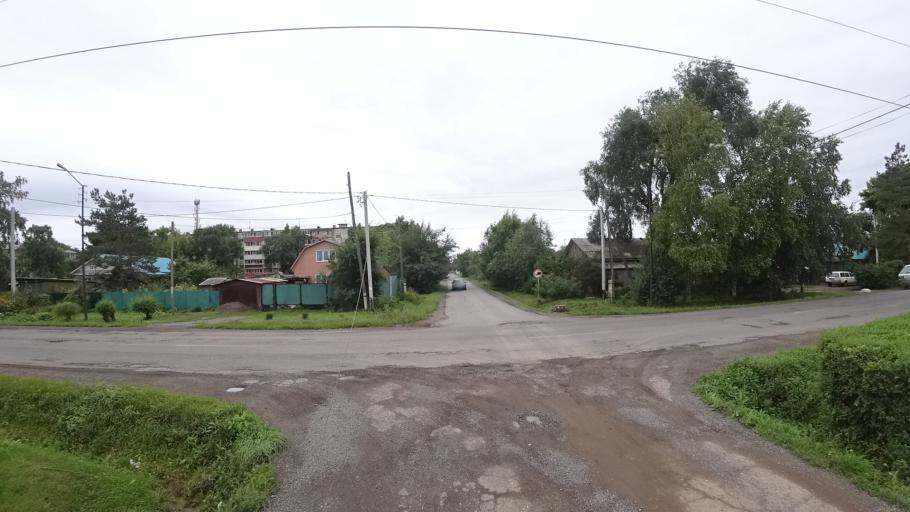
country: RU
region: Primorskiy
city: Chernigovka
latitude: 44.3465
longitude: 132.5748
